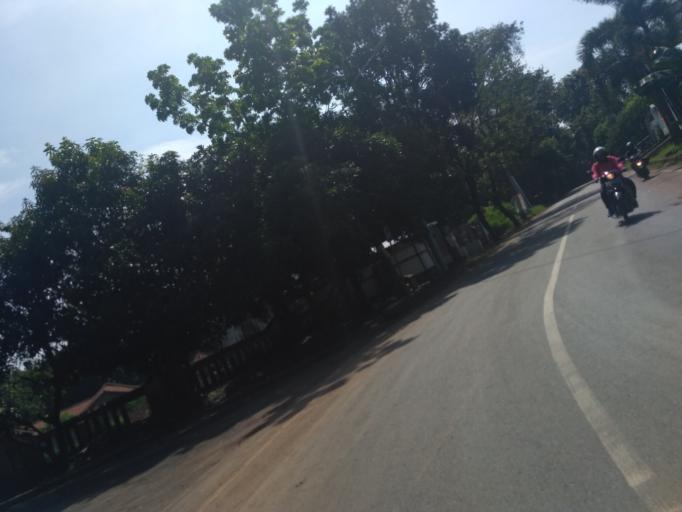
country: ID
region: Central Java
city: Semarang
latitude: -7.0255
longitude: 110.4115
